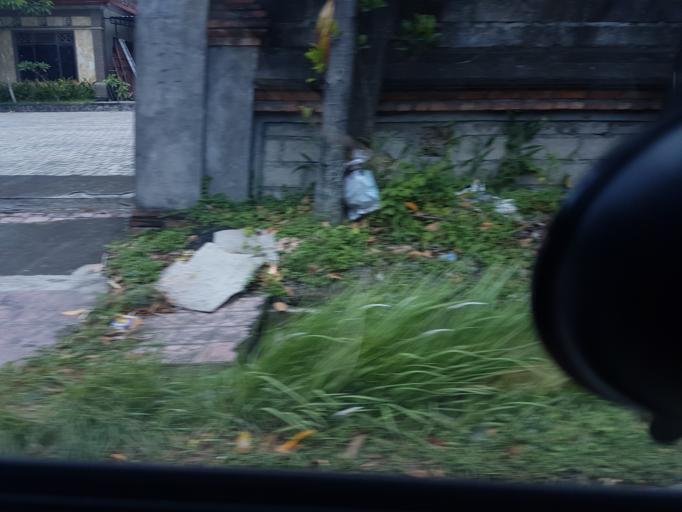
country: ID
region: Bali
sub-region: Kabupaten Gianyar
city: Ubud
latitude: -8.5315
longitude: 115.2720
